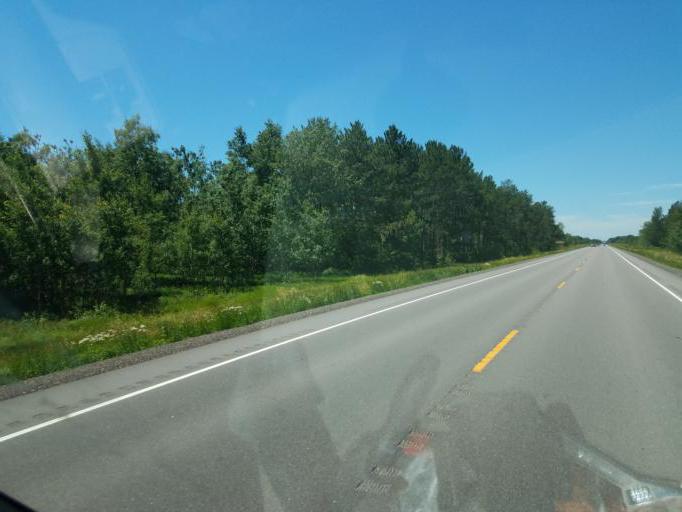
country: US
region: Wisconsin
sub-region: Juneau County
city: New Lisbon
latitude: 44.0246
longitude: -90.1137
